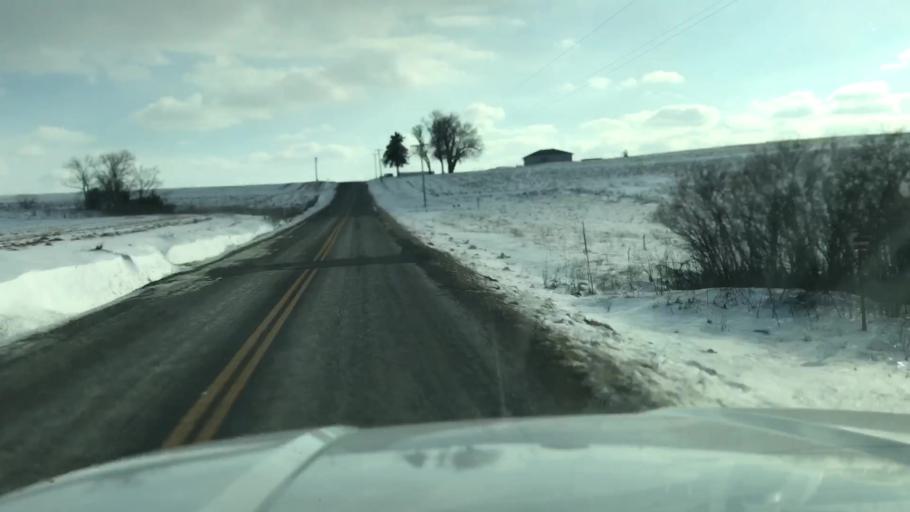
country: US
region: Missouri
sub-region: Nodaway County
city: Maryville
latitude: 40.1904
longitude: -95.0121
